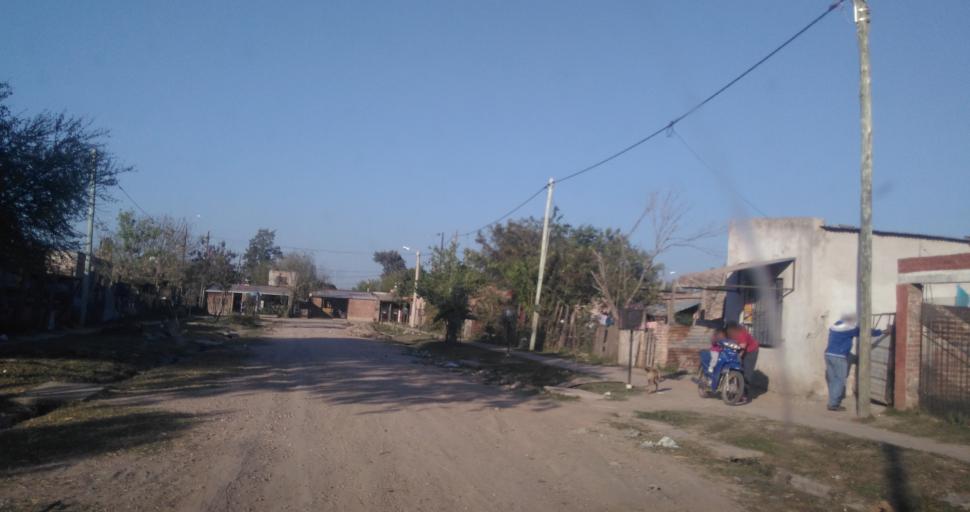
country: AR
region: Chaco
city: Resistencia
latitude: -27.4789
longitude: -59.0097
